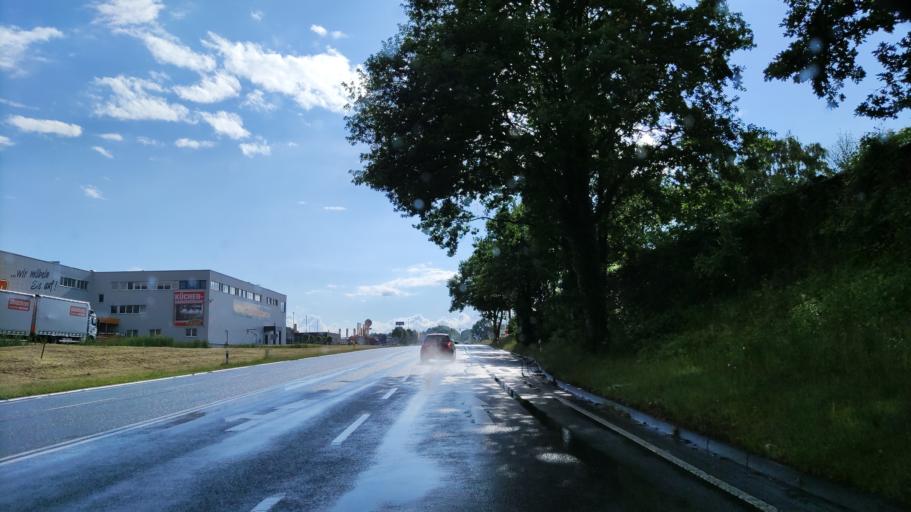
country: DE
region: Lower Saxony
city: Stade
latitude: 53.5950
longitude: 9.4275
